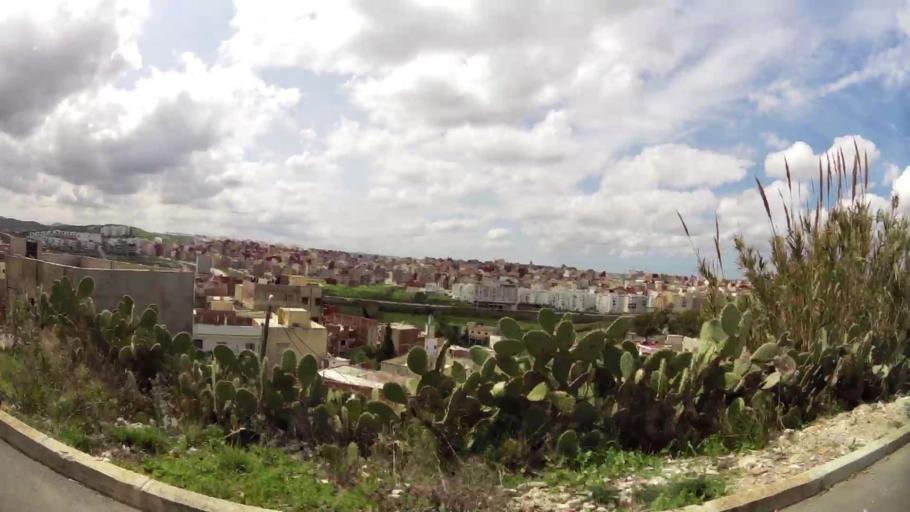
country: MA
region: Tanger-Tetouan
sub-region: Tanger-Assilah
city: Tangier
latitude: 35.7705
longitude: -5.7564
